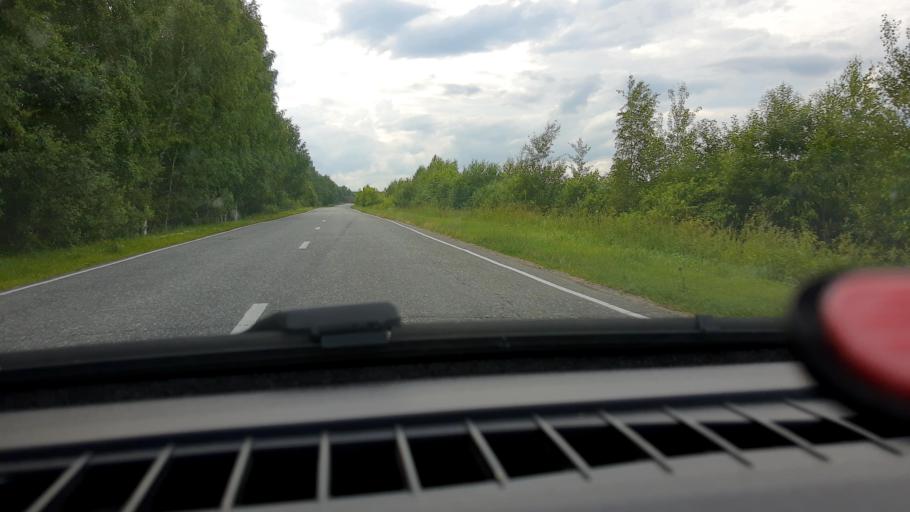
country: RU
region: Nizjnij Novgorod
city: Neklyudovo
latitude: 56.5201
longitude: 43.8910
